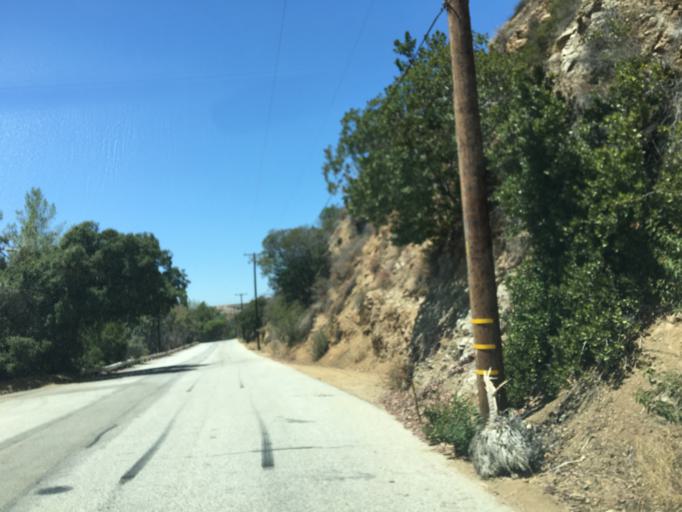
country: US
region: California
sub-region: Los Angeles County
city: Glendora
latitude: 34.1564
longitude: -117.8345
